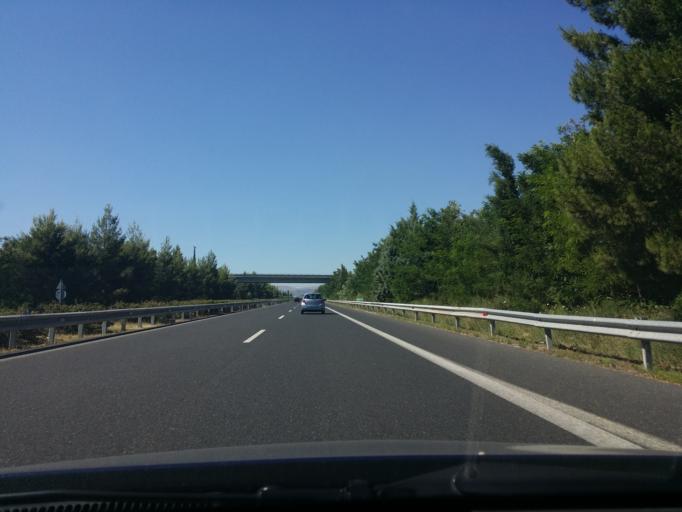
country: GR
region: Peloponnese
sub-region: Nomos Arkadias
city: Tripoli
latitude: 37.5197
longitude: 22.4069
